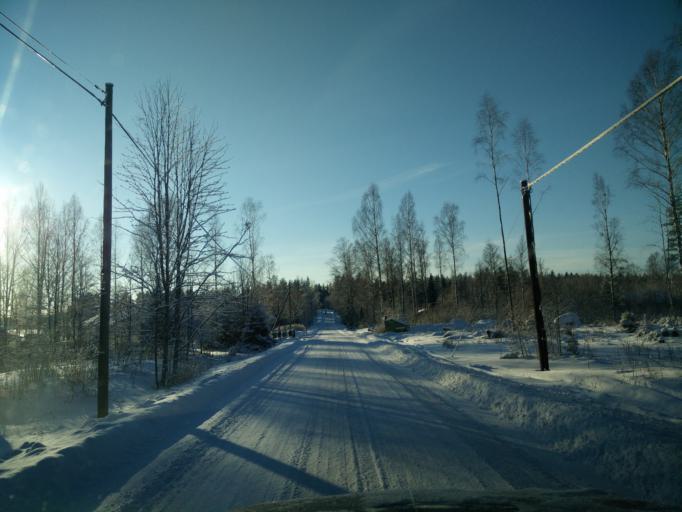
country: SE
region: Vaesternorrland
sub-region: Sundsvalls Kommun
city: Njurundabommen
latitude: 62.2301
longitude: 17.5029
